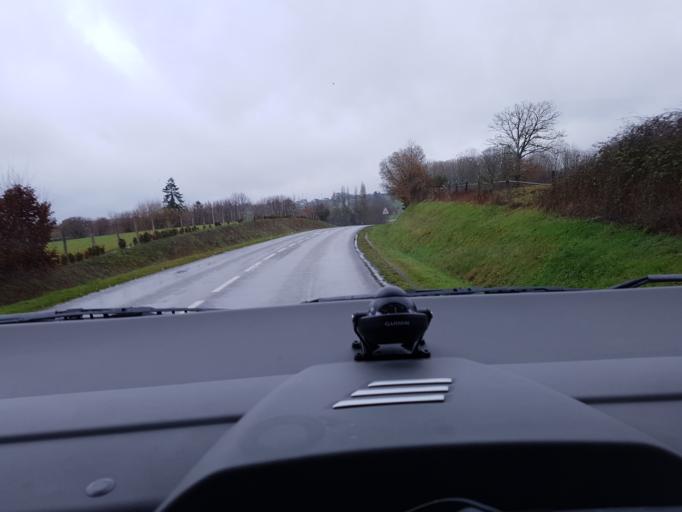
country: FR
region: Pays de la Loire
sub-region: Departement de la Mayenne
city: Gorron
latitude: 48.4154
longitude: -0.8228
